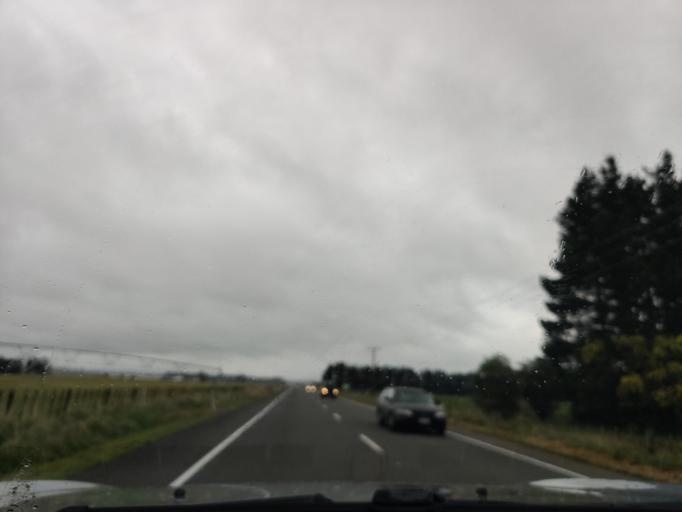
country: NZ
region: Hawke's Bay
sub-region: Hastings District
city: Hastings
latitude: -40.0139
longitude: 176.3647
